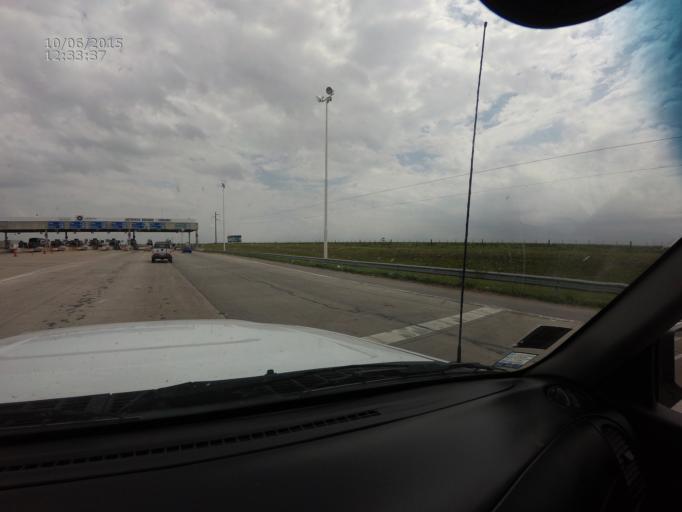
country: AR
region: Santa Fe
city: Carcarana
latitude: -32.8764
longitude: -61.1689
